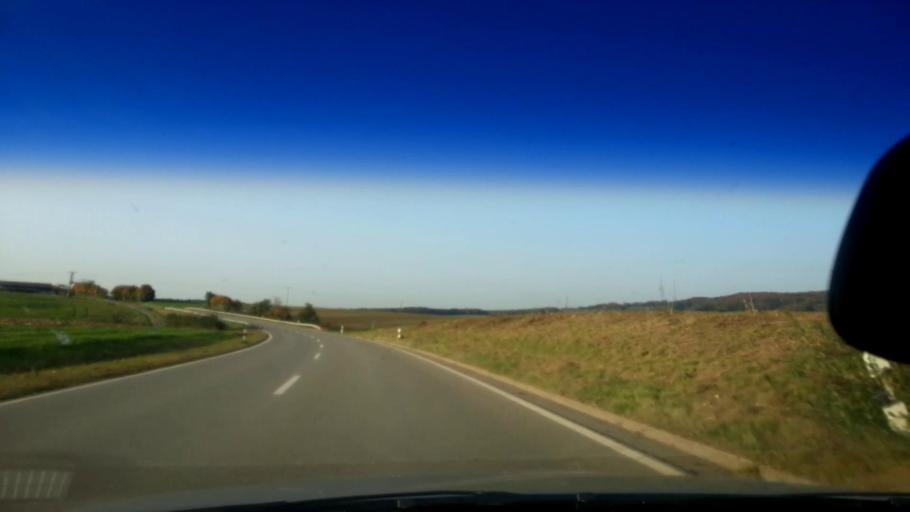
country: DE
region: Bavaria
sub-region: Upper Franconia
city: Schesslitz
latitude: 49.9956
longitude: 11.0235
